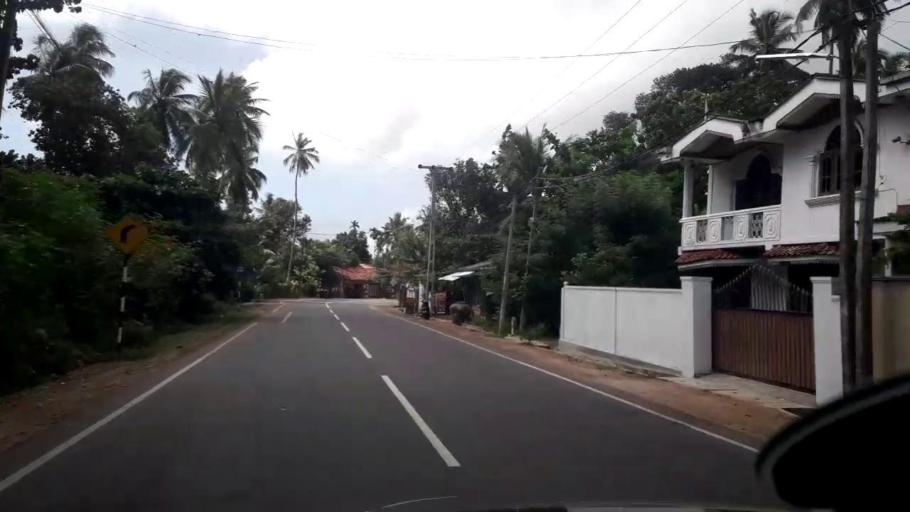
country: LK
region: Western
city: Panadura
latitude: 6.6683
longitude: 79.9377
